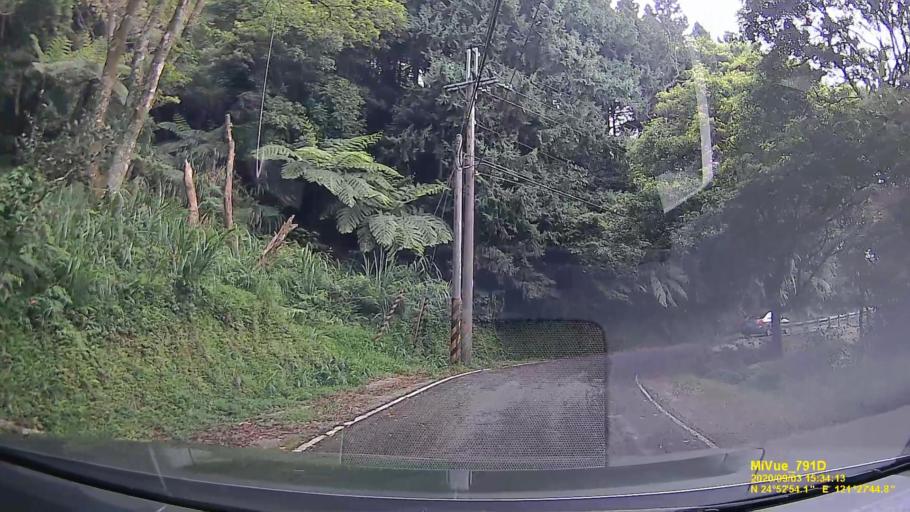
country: TW
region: Taipei
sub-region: Taipei
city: Banqiao
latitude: 24.8817
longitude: 121.4625
